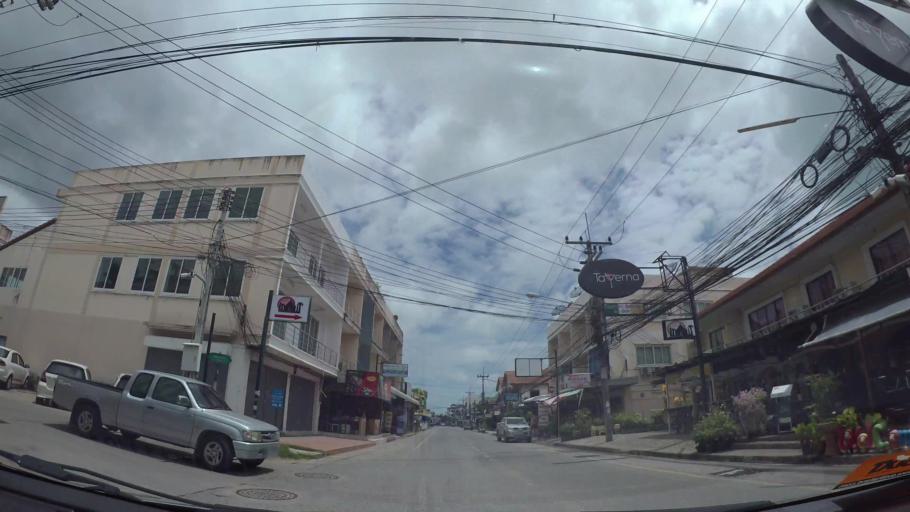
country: TH
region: Chon Buri
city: Sattahip
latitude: 12.7618
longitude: 100.8976
